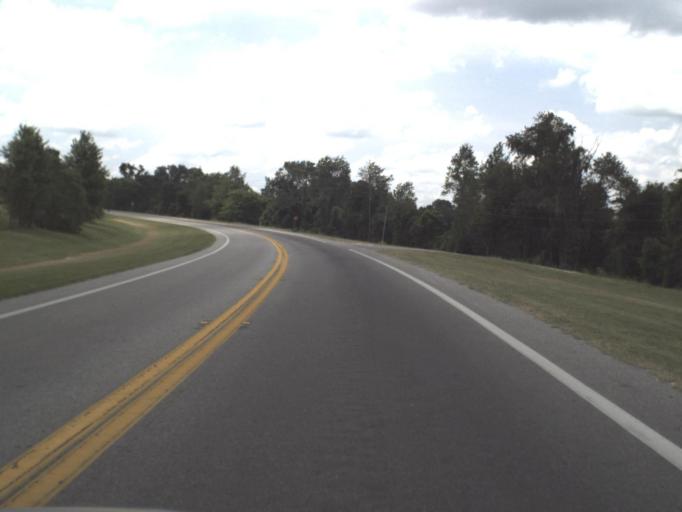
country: US
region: Florida
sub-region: Hamilton County
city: Jasper
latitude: 30.5073
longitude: -82.9458
